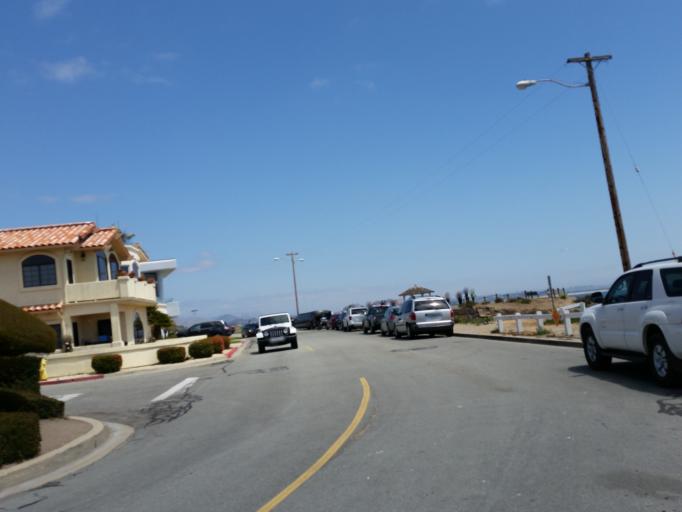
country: US
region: California
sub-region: San Luis Obispo County
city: Pismo Beach
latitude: 35.1527
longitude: -120.6694
